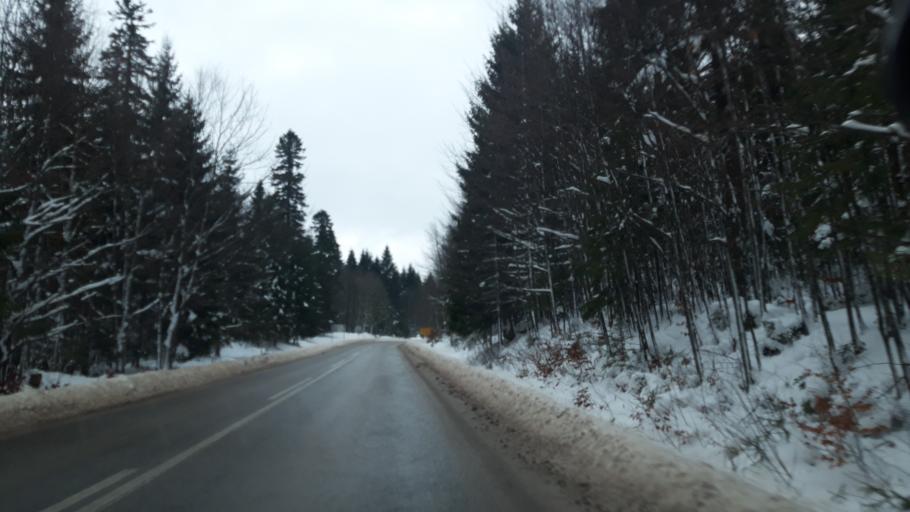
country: BA
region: Republika Srpska
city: Han Pijesak
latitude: 44.0676
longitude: 18.9458
